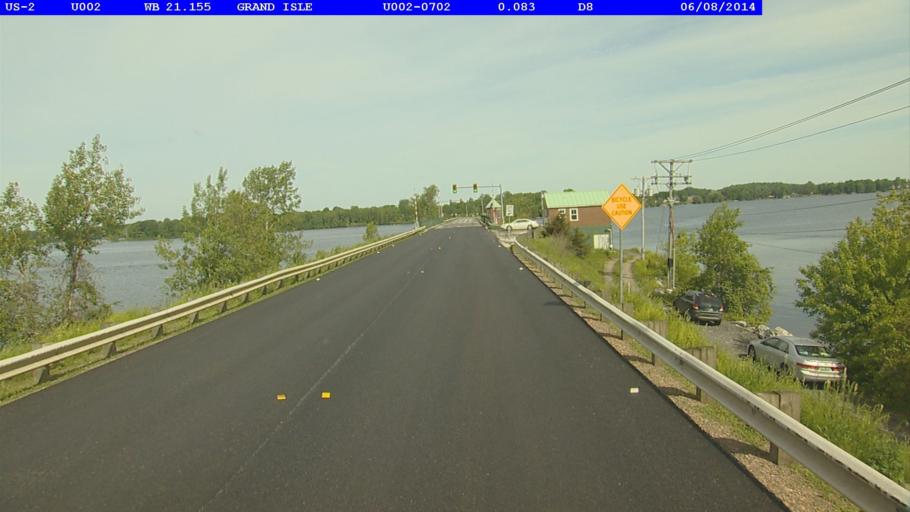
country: US
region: Vermont
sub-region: Grand Isle County
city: North Hero
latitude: 44.7652
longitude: -73.2888
